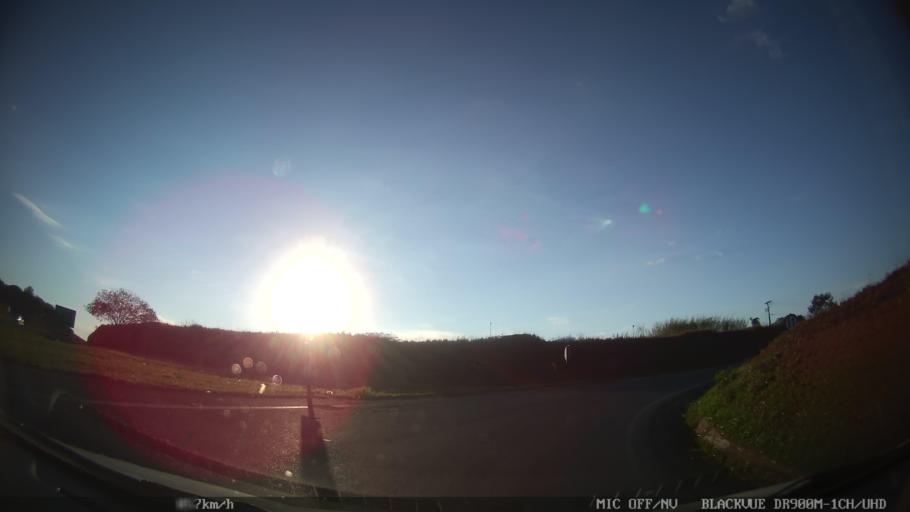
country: BR
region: Sao Paulo
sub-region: Piracicaba
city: Piracicaba
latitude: -22.7232
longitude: -47.5853
